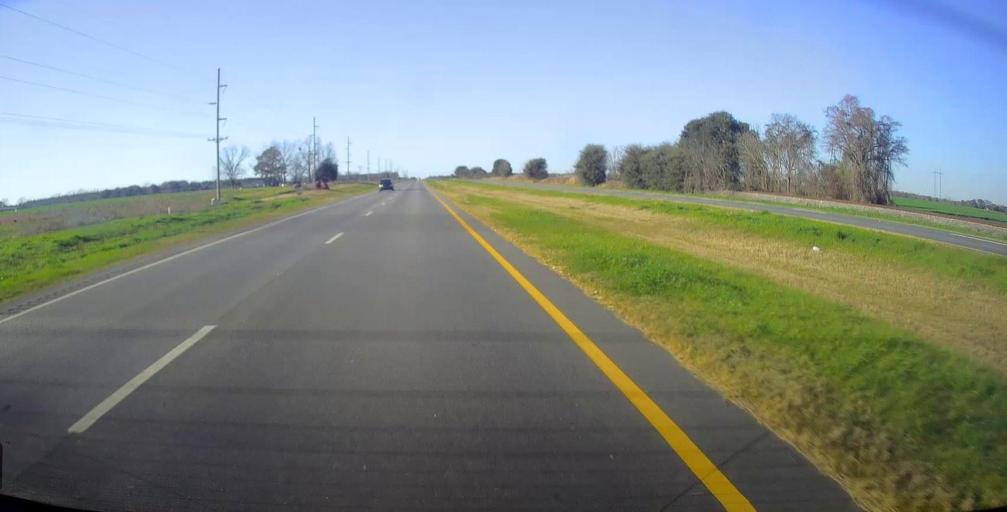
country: US
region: Georgia
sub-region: Lee County
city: Leesburg
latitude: 31.7726
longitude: -84.1914
